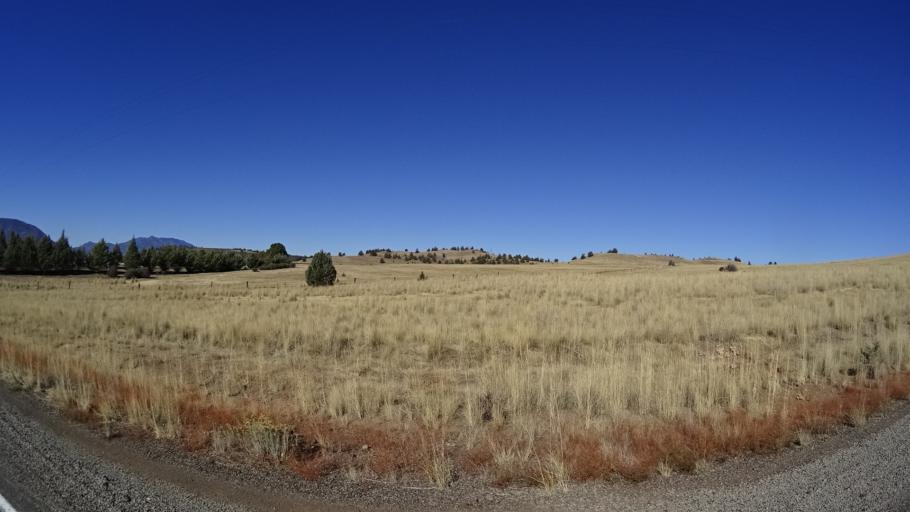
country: US
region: California
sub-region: Siskiyou County
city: Montague
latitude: 41.9010
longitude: -122.3904
